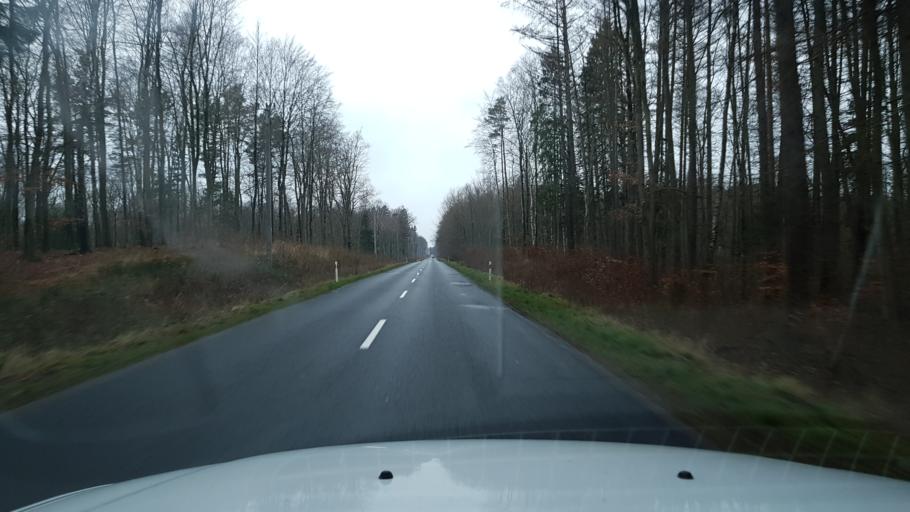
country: PL
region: West Pomeranian Voivodeship
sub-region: Powiat gryficki
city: Trzebiatow
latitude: 54.0561
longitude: 15.3515
